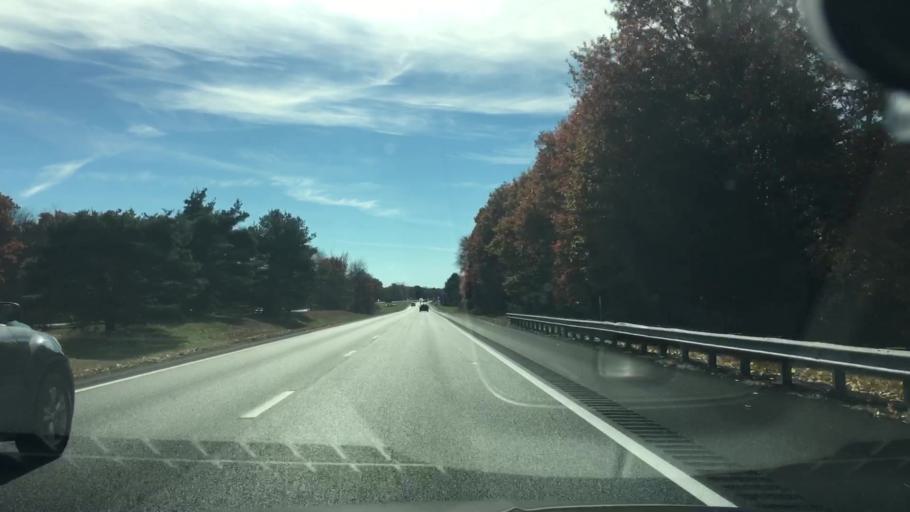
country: US
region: Massachusetts
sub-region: Hampshire County
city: Hatfield
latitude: 42.3762
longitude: -72.6327
